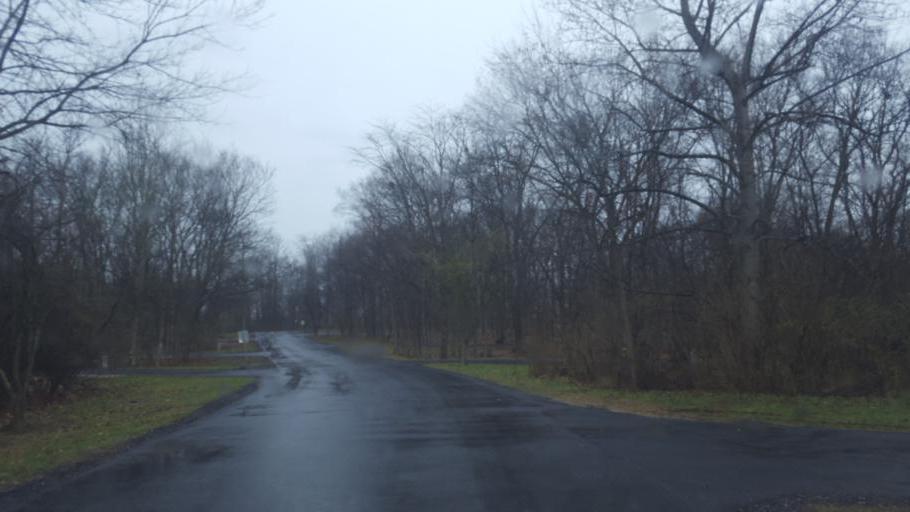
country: US
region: Ohio
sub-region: Delaware County
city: Lewis Center
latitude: 40.2368
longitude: -82.9845
